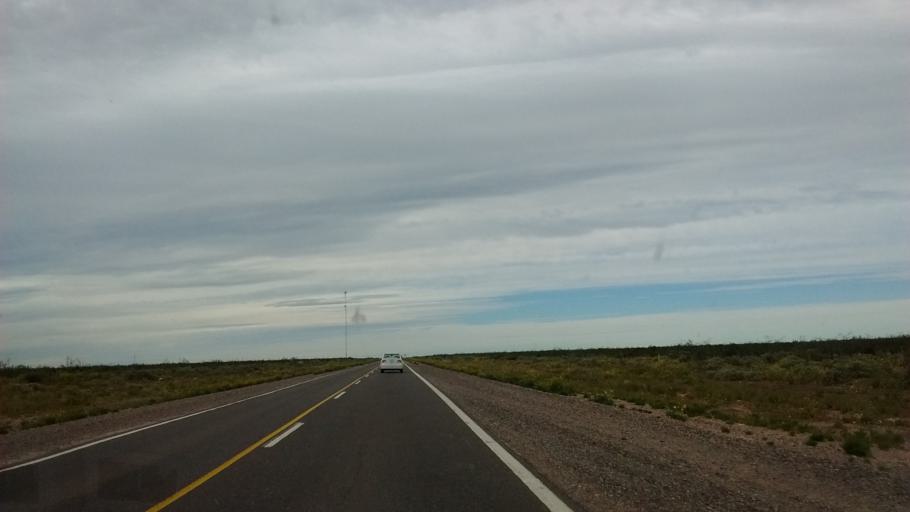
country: AR
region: Rio Negro
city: Contraalmirante Cordero
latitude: -38.3146
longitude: -68.0043
